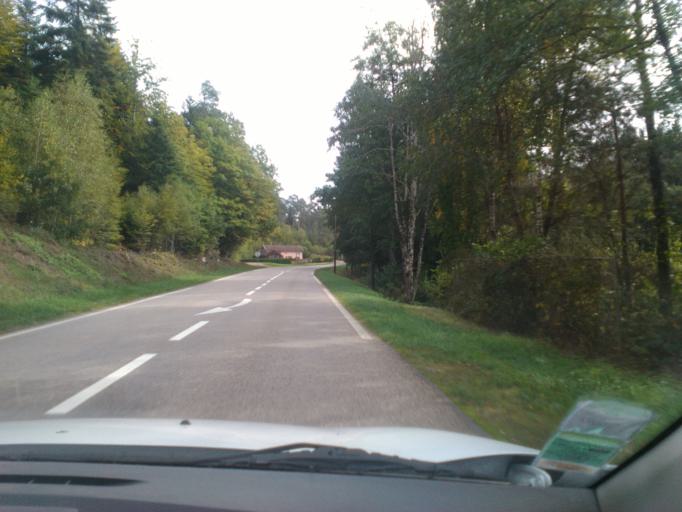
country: FR
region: Lorraine
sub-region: Departement des Vosges
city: Jeanmenil
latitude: 48.3246
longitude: 6.7333
